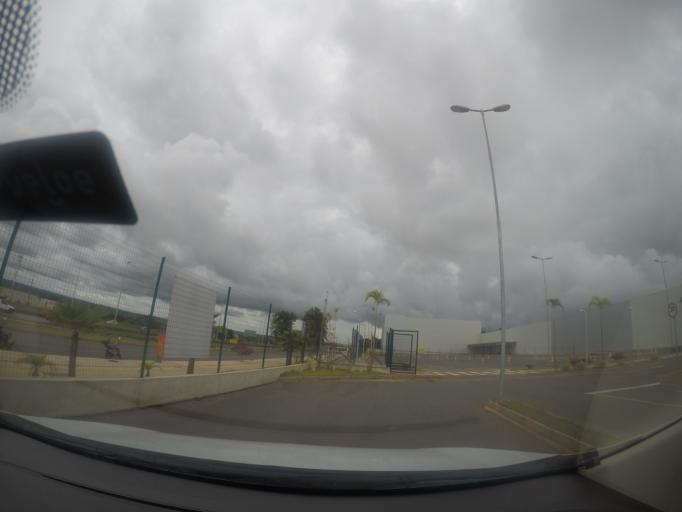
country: BR
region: Goias
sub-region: Trindade
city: Trindade
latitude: -16.6553
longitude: -49.3842
